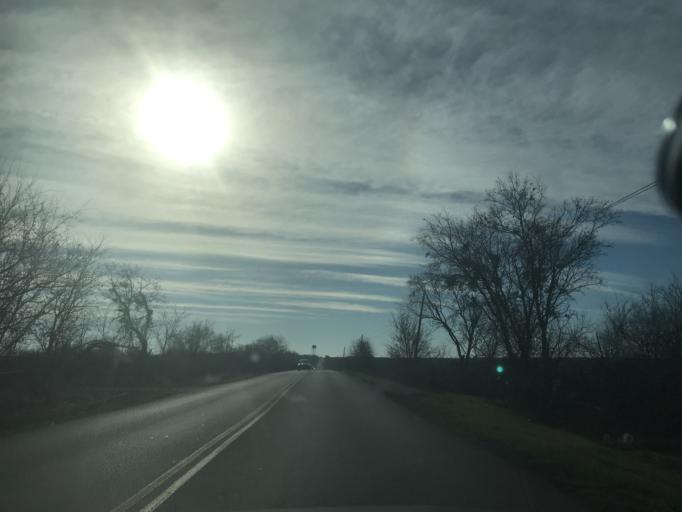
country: US
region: Texas
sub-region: Travis County
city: Manor
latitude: 30.3281
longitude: -97.5467
